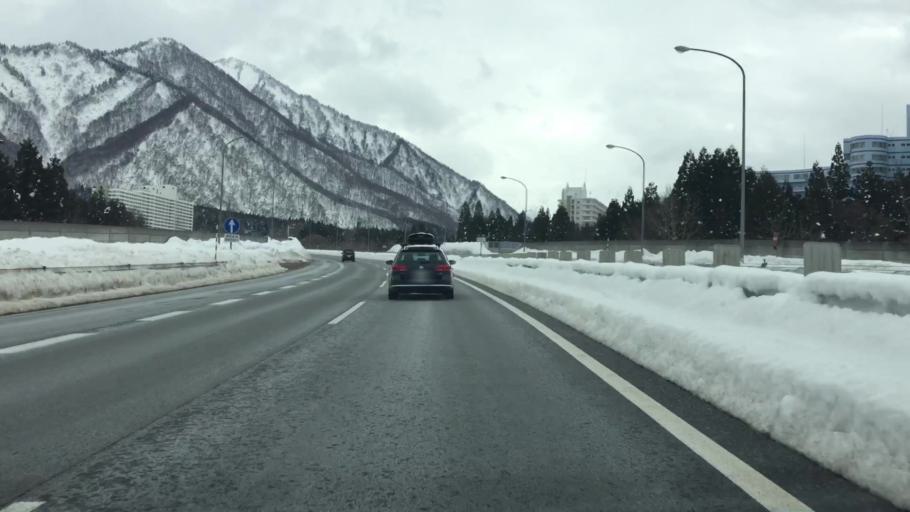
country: JP
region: Niigata
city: Shiozawa
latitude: 36.9092
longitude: 138.8413
